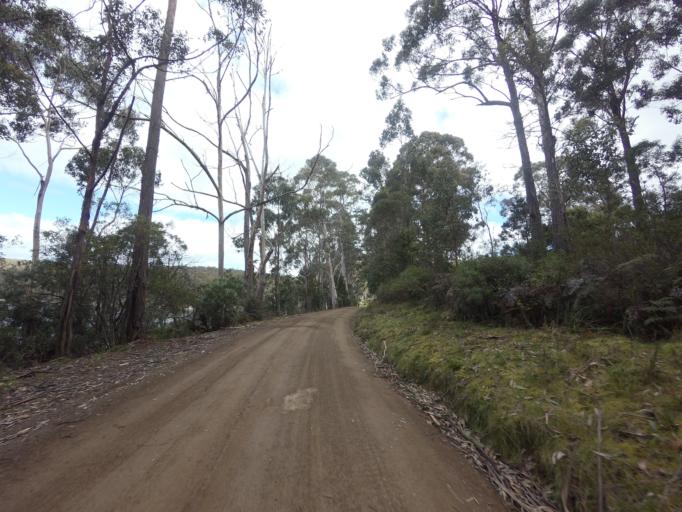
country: AU
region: Tasmania
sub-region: Huon Valley
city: Geeveston
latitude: -43.4201
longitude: 147.0137
